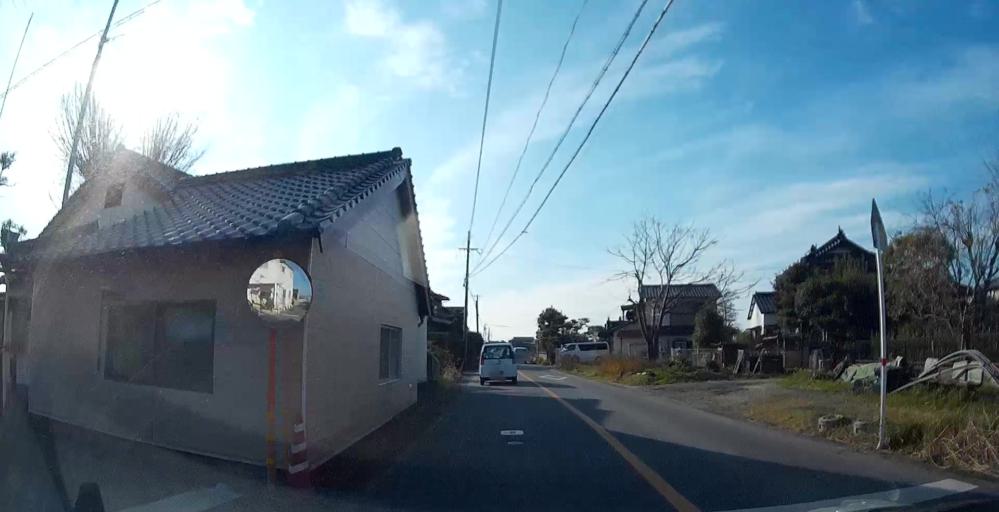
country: JP
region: Kumamoto
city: Uto
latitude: 32.7331
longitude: 130.6494
